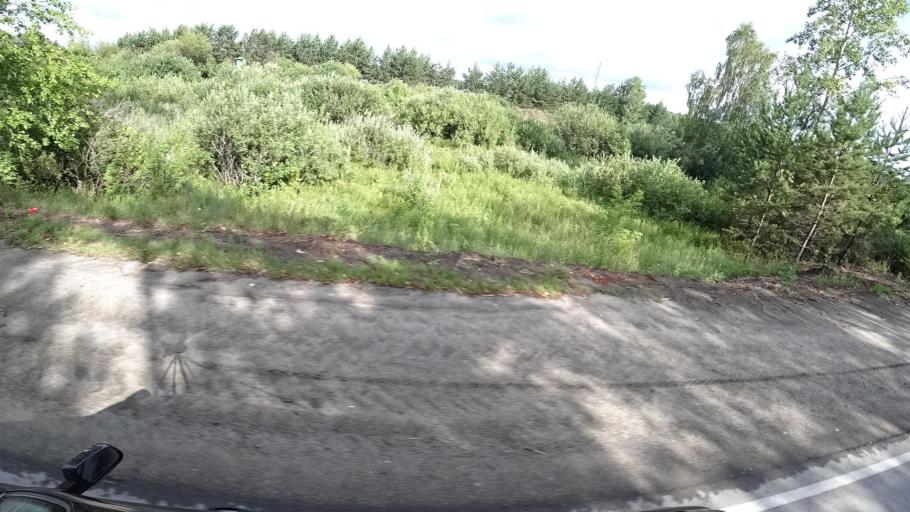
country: RU
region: Sverdlovsk
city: Kamyshlov
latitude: 56.8354
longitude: 62.6971
